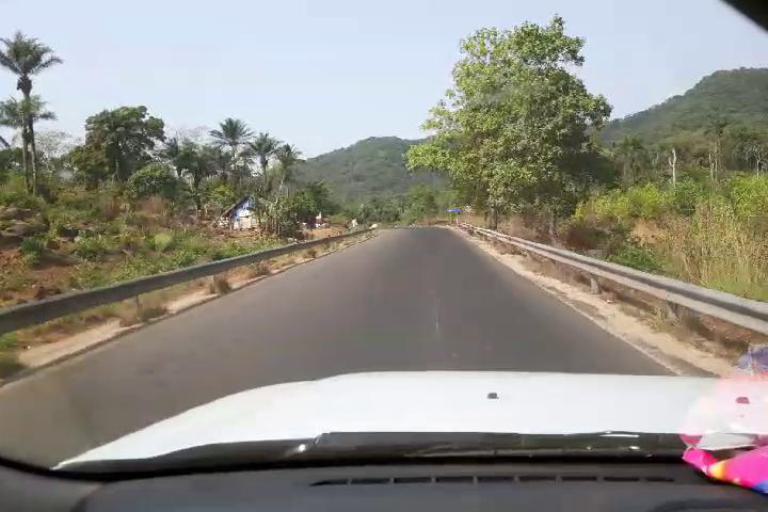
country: SL
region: Western Area
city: Hastings
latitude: 8.2718
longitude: -13.1585
